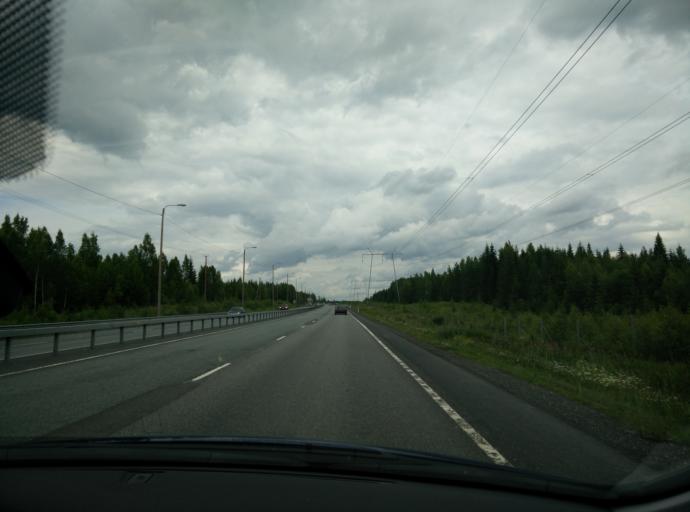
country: FI
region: Pirkanmaa
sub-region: Tampere
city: Kangasala
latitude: 61.6086
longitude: 24.1434
